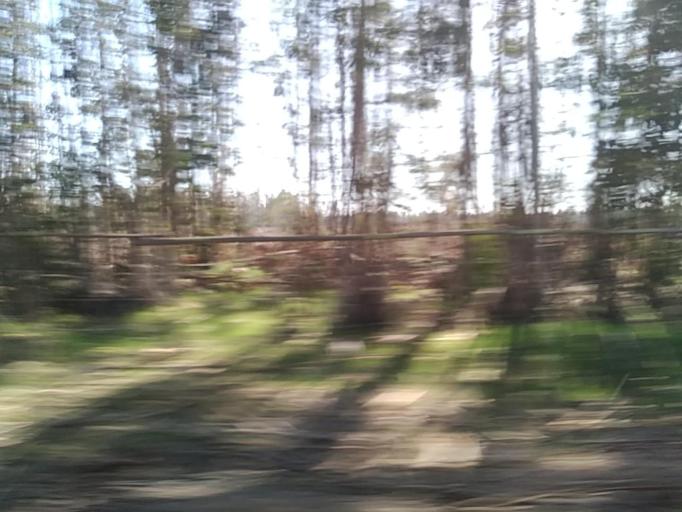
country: CL
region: Valparaiso
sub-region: San Antonio Province
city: El Tabo
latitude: -33.4108
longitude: -71.6065
